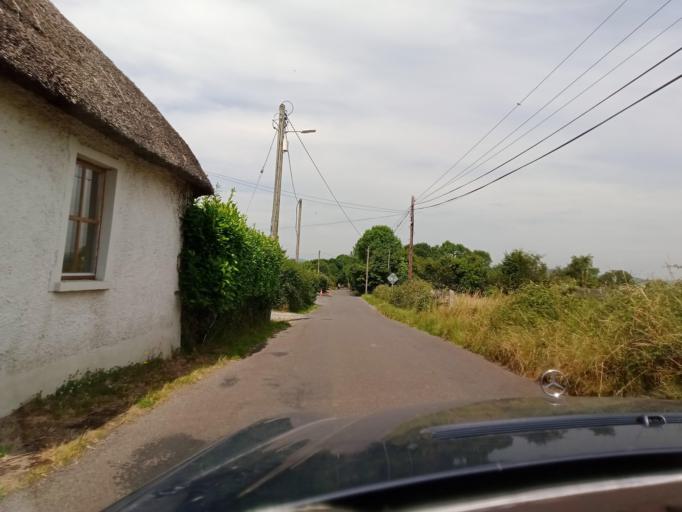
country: IE
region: Leinster
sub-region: Kilkenny
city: Mooncoin
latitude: 52.2720
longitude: -7.2164
